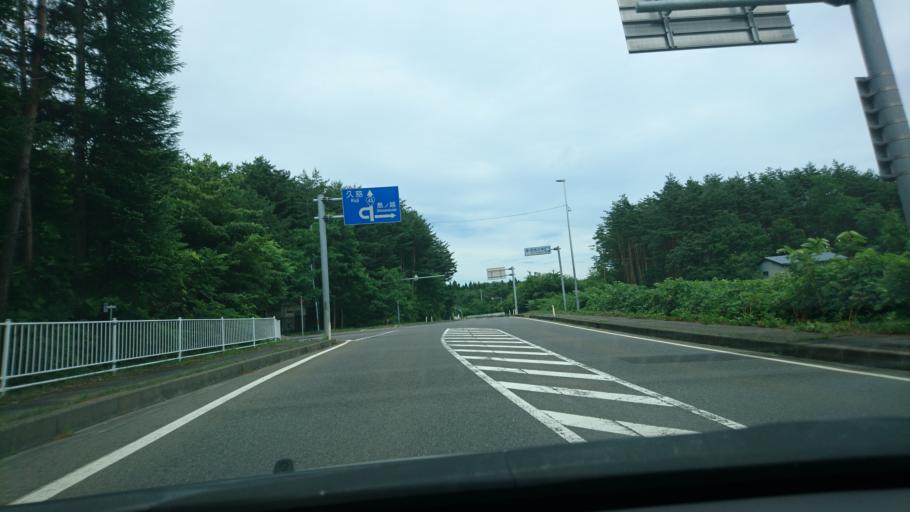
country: JP
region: Iwate
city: Miyako
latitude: 39.9128
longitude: 141.9029
